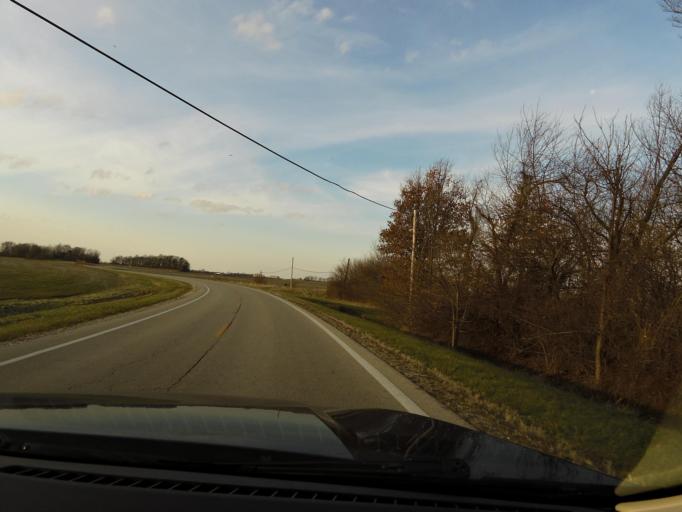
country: US
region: Illinois
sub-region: Fayette County
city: Vandalia
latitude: 38.9556
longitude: -89.1311
